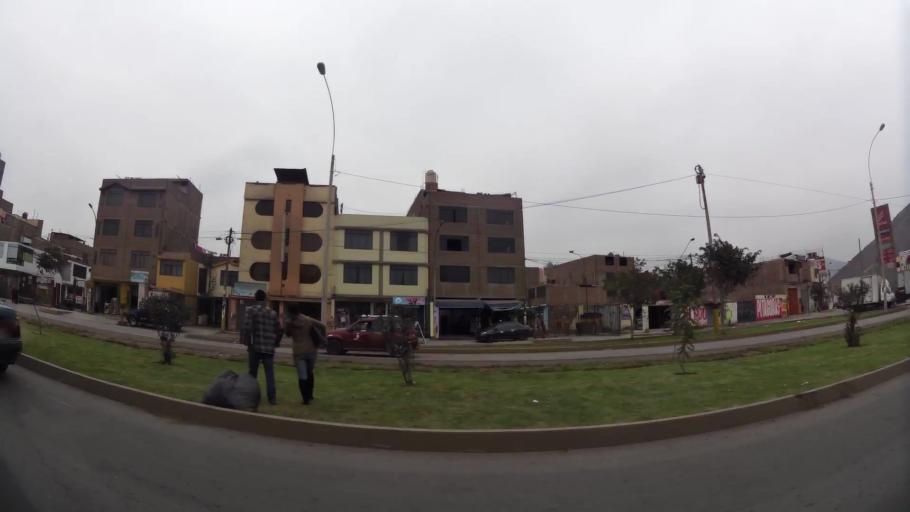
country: PE
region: Lima
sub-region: Lima
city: Vitarte
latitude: -12.0394
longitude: -76.9235
